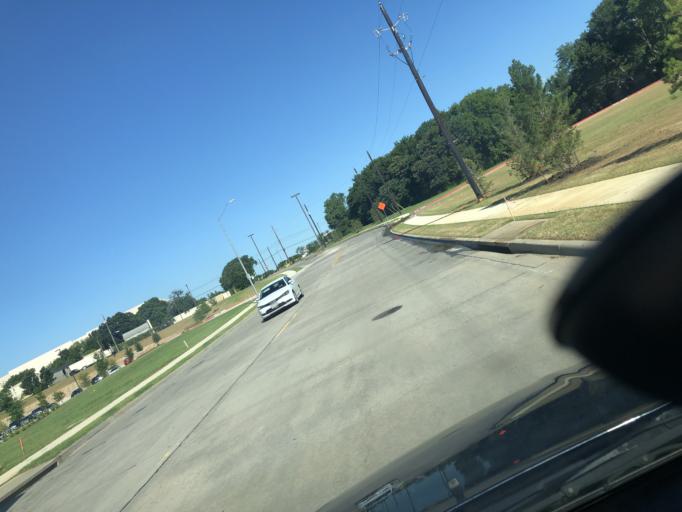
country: US
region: Texas
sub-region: Tarrant County
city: Euless
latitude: 32.8219
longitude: -97.0285
